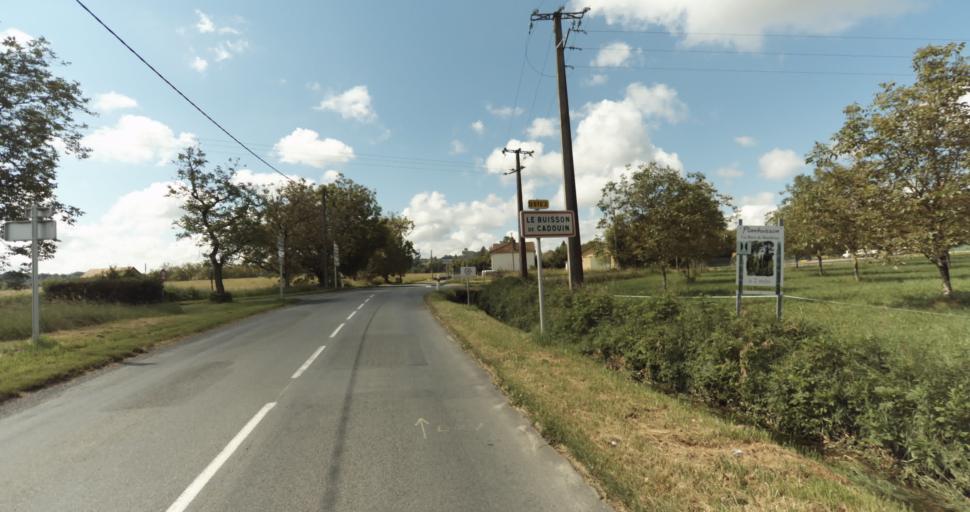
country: FR
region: Aquitaine
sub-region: Departement de la Dordogne
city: Le Bugue
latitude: 44.8524
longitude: 0.9105
